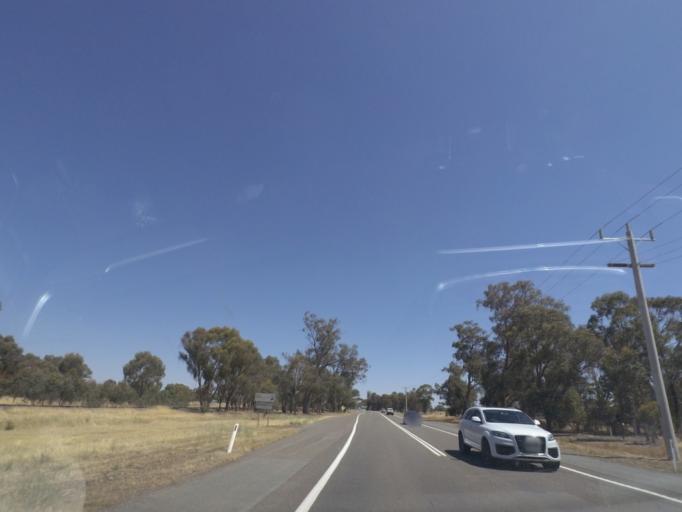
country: AU
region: Victoria
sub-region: Greater Shepparton
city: Shepparton
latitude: -36.2349
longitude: 145.4317
